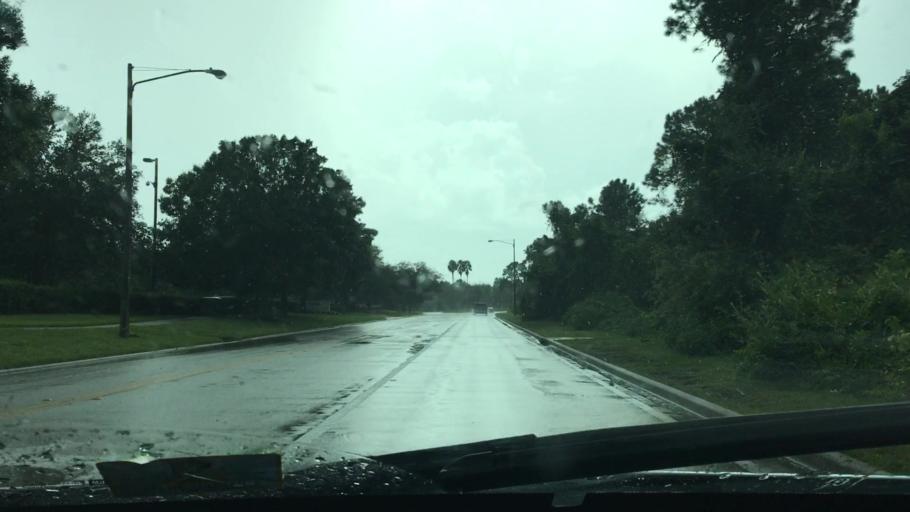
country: US
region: Florida
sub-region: Orange County
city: Alafaya
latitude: 28.6065
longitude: -81.2144
